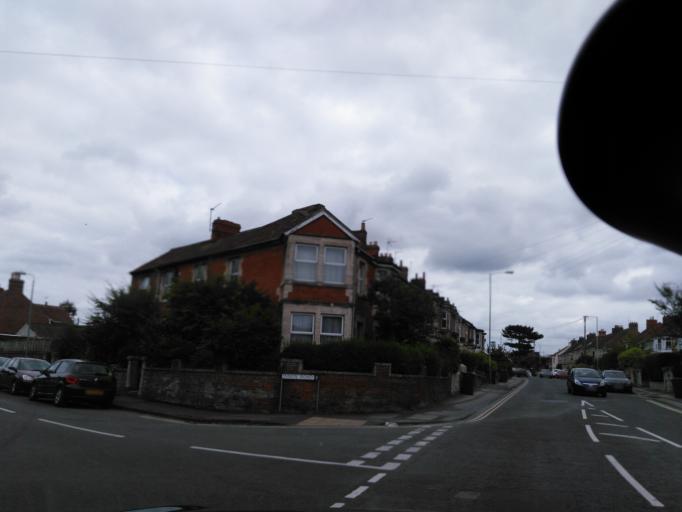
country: GB
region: England
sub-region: Wiltshire
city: Trowbridge
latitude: 51.3210
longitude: -2.2192
